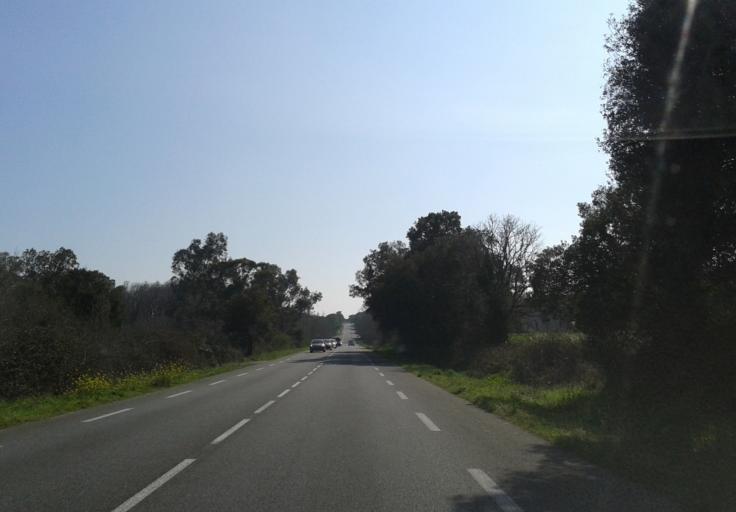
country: FR
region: Corsica
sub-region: Departement de la Haute-Corse
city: Linguizzetta
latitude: 42.2345
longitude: 9.5455
